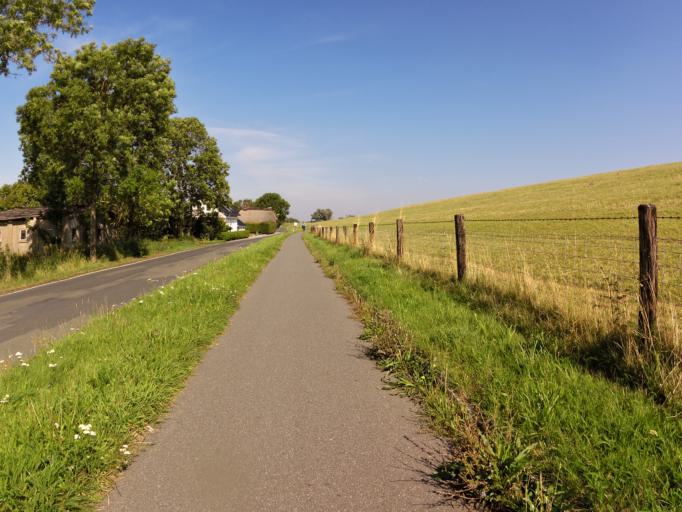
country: DE
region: Lower Saxony
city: Elsfleth
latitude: 53.2796
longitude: 8.4812
